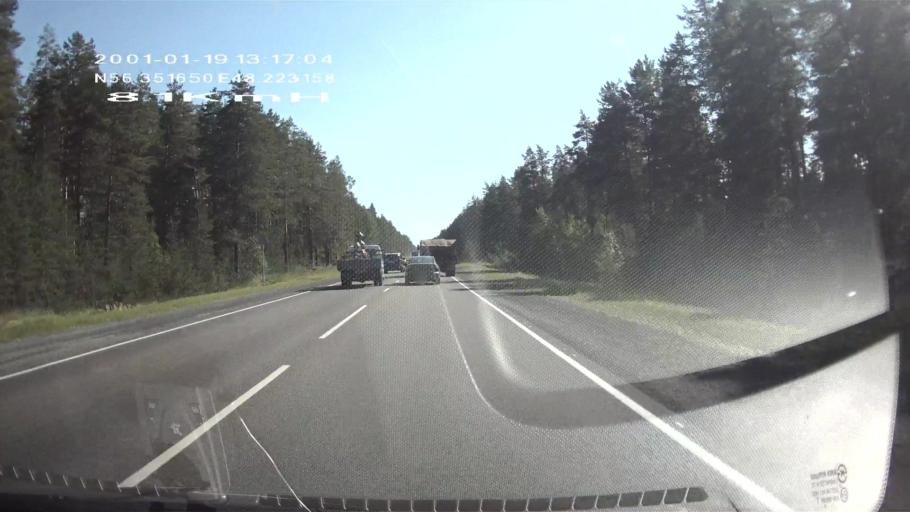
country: RU
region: Mariy-El
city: Suslonger
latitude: 56.3515
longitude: 48.2233
